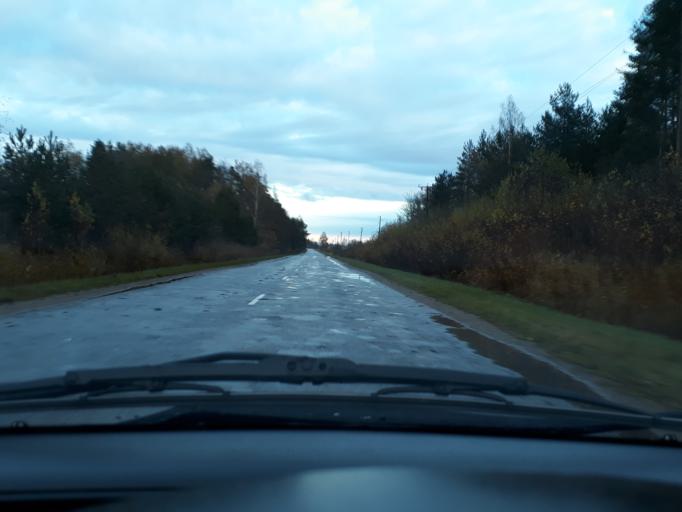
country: LV
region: Dobeles Rajons
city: Dobele
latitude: 56.6142
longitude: 23.2500
